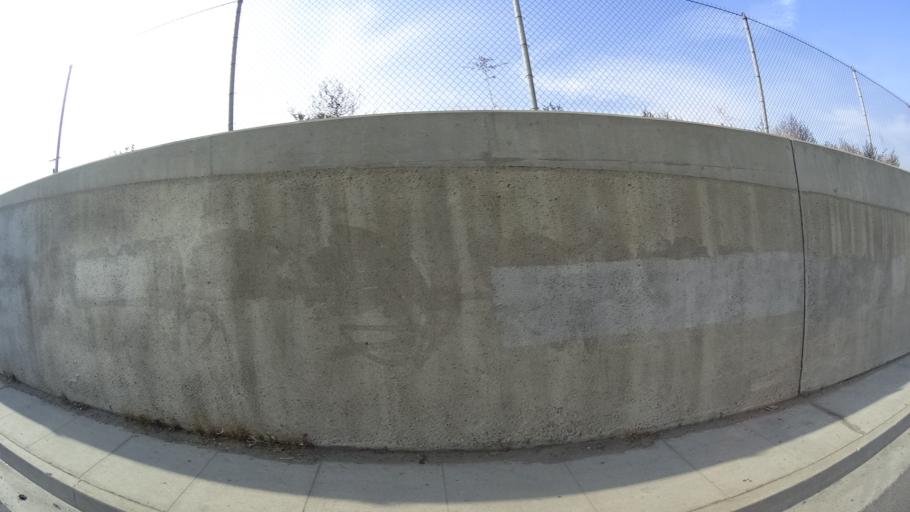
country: US
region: California
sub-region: Kern County
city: Bakersfield
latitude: 35.3718
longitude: -119.0031
